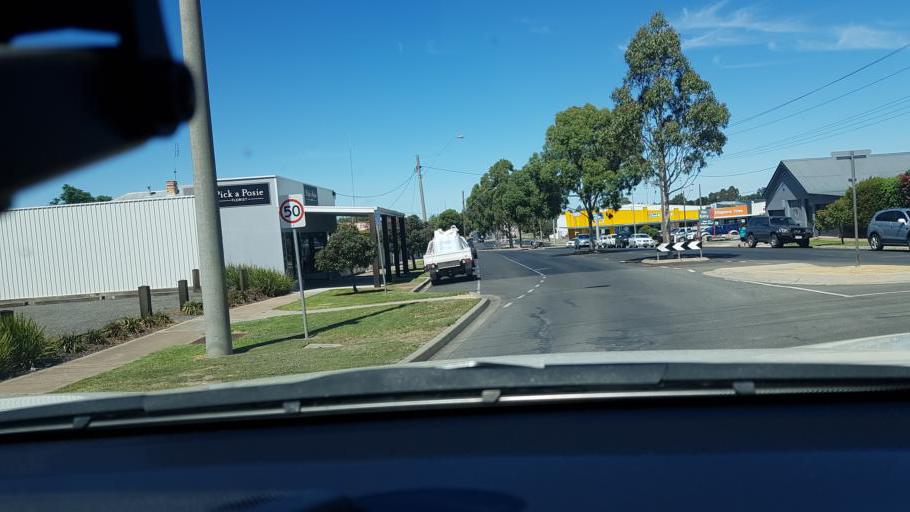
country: AU
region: Victoria
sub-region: Horsham
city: Horsham
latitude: -36.7153
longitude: 142.2023
